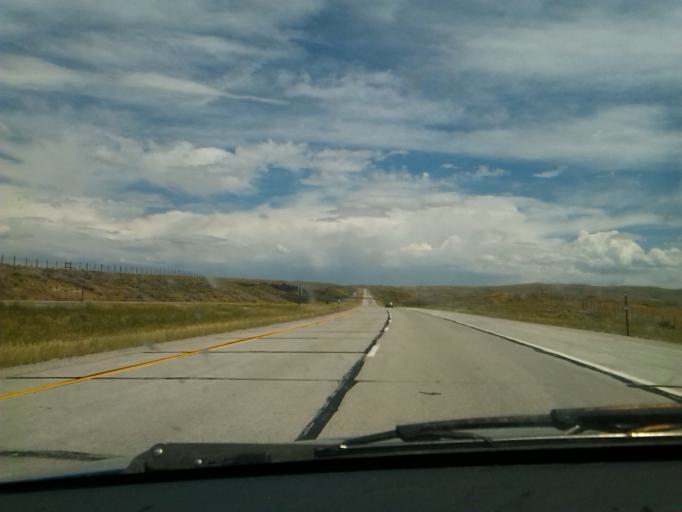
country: US
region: Wyoming
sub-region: Carbon County
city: Saratoga
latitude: 41.7304
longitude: -106.7007
